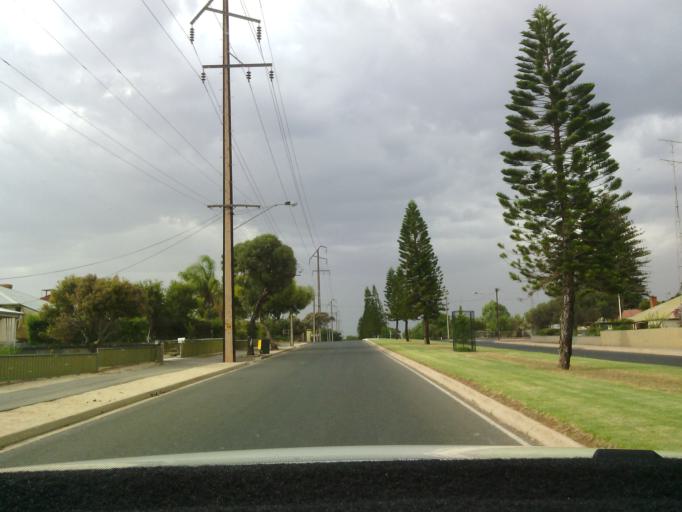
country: AU
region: South Australia
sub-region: Berri and Barmera
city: Berri
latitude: -34.2770
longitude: 140.5973
